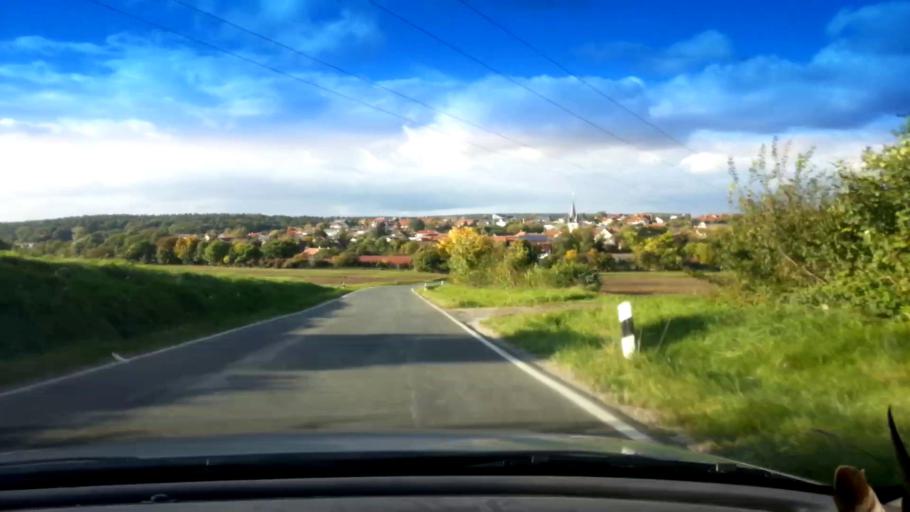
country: DE
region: Bavaria
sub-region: Upper Franconia
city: Strullendorf
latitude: 49.8506
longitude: 11.0019
